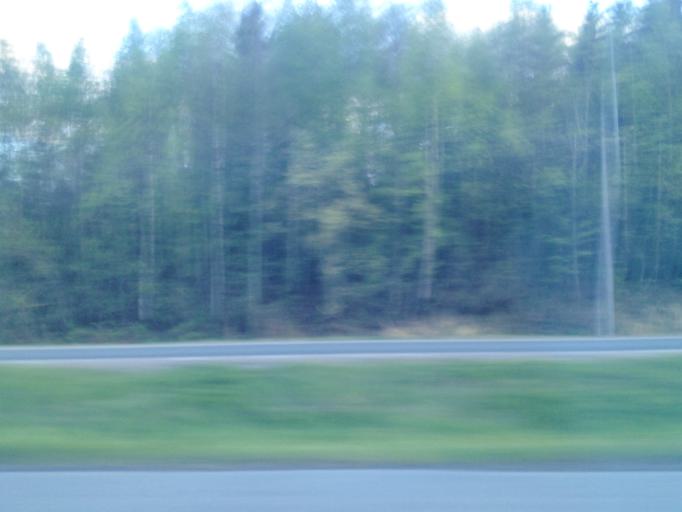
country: FI
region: Haeme
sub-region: Haemeenlinna
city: Kalvola
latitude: 61.0962
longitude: 24.1709
